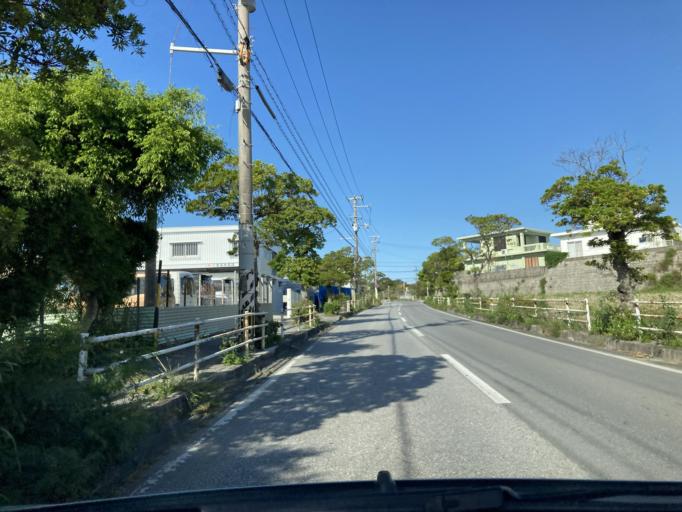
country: JP
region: Okinawa
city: Tomigusuku
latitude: 26.1766
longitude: 127.7057
